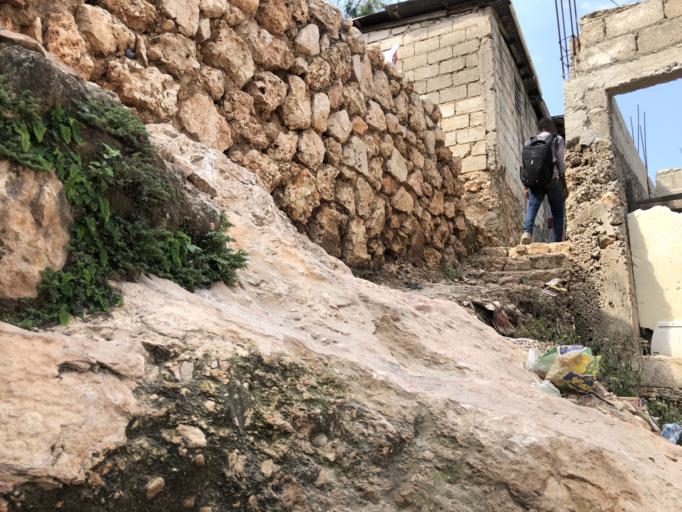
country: HT
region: Ouest
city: Port-au-Prince
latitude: 18.5204
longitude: -72.3172
